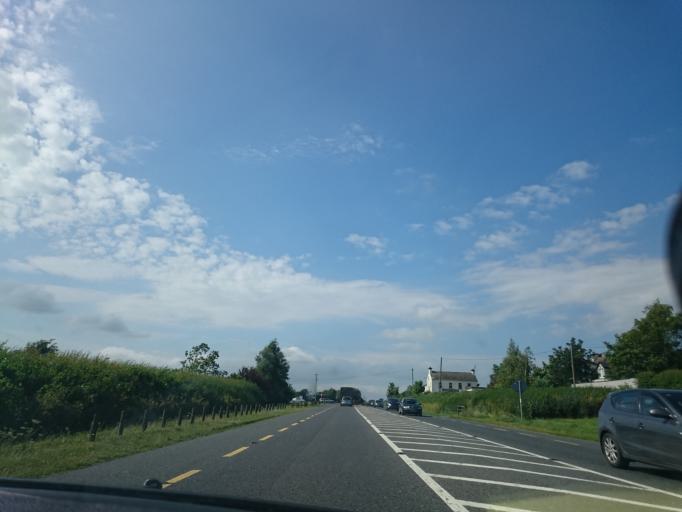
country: IE
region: Leinster
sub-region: Kilkenny
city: Kilkenny
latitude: 52.5818
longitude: -7.2383
